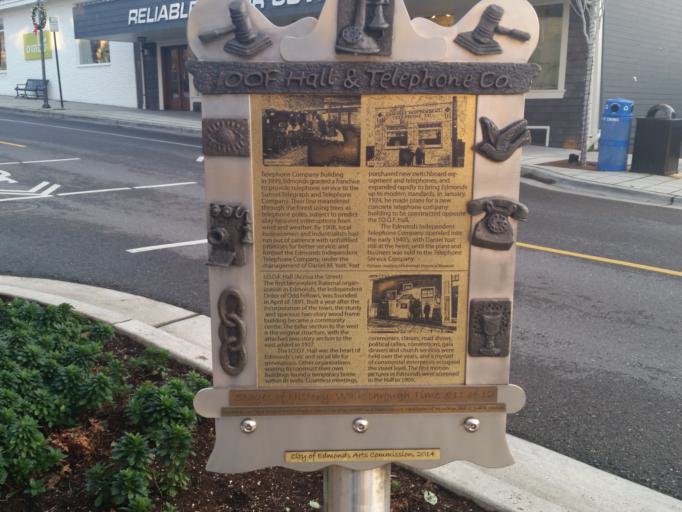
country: US
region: Washington
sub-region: Snohomish County
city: Edmonds
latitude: 47.8107
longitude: -122.3760
